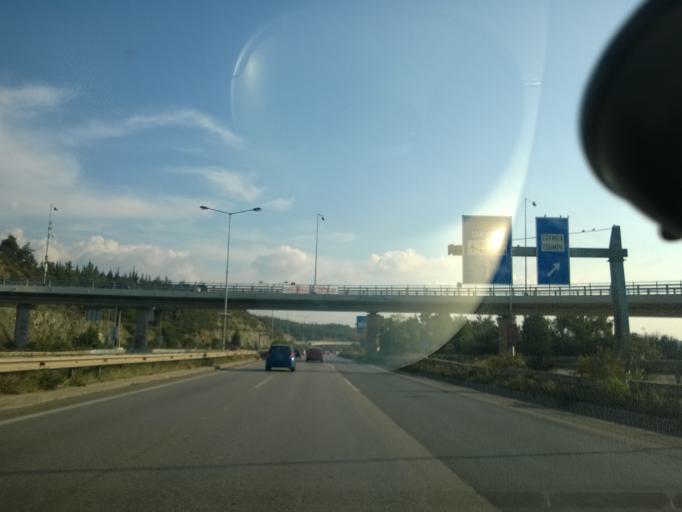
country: GR
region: Central Macedonia
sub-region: Nomos Thessalonikis
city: Triandria
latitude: 40.6260
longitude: 22.9793
